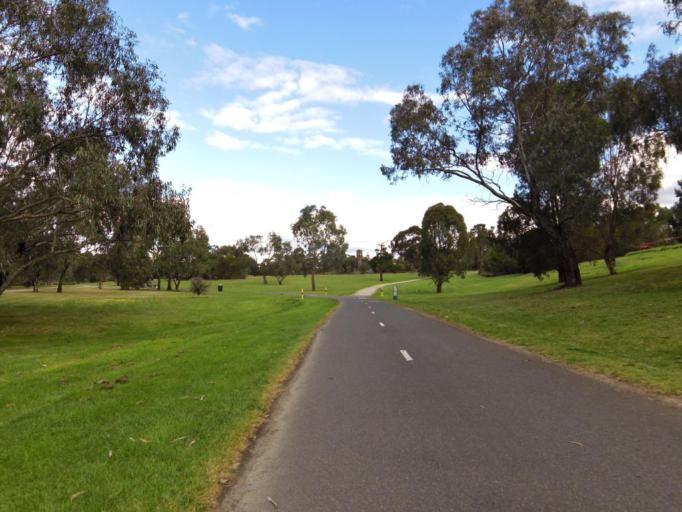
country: AU
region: Victoria
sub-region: Boroondara
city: Balwyn North
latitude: -37.7816
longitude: 145.0959
